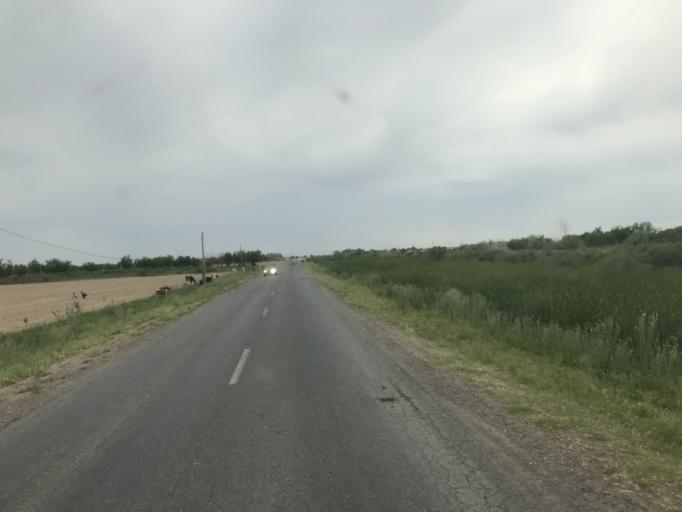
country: KZ
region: Ongtustik Qazaqstan
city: Asykata
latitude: 40.9216
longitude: 68.4004
